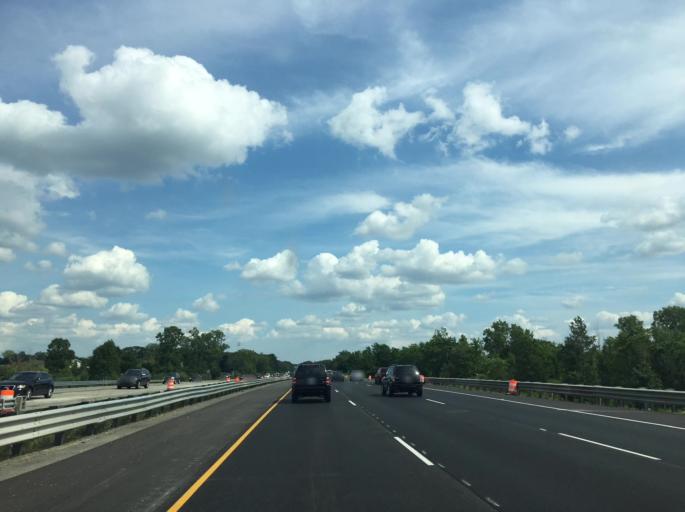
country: US
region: Michigan
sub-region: Oakland County
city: Waterford
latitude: 42.7206
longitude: -83.3490
